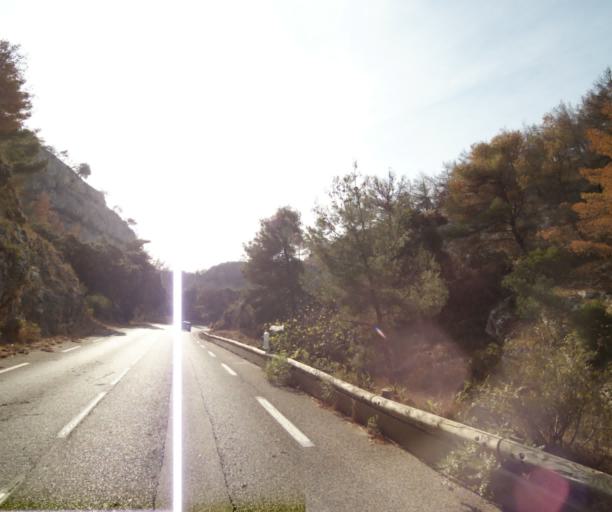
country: FR
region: Provence-Alpes-Cote d'Azur
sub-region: Departement des Bouches-du-Rhone
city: Ensues-la-Redonne
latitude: 43.3444
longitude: 5.1810
